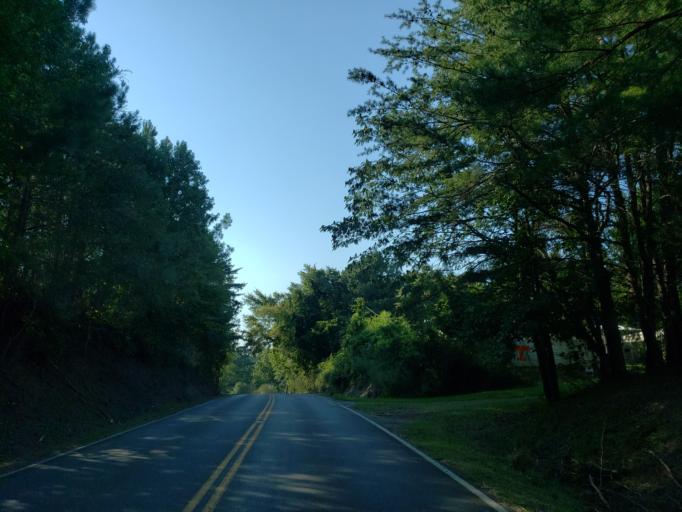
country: US
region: Tennessee
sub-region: Bradley County
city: Wildwood Lake
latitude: 35.0667
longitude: -84.7683
